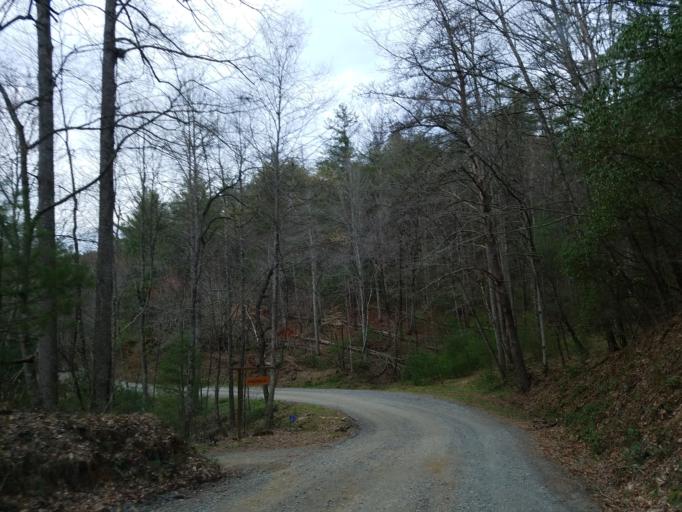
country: US
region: Georgia
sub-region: Fannin County
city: Blue Ridge
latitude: 34.7490
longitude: -84.2665
